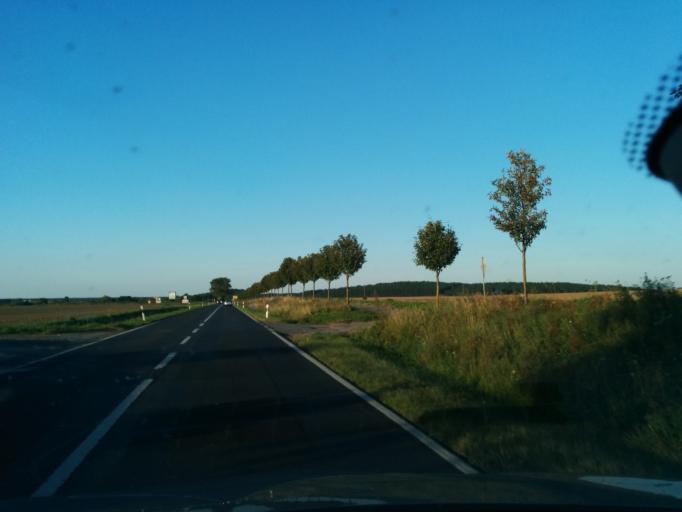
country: DE
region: Mecklenburg-Vorpommern
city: Loddin
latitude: 53.9491
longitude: 14.0501
